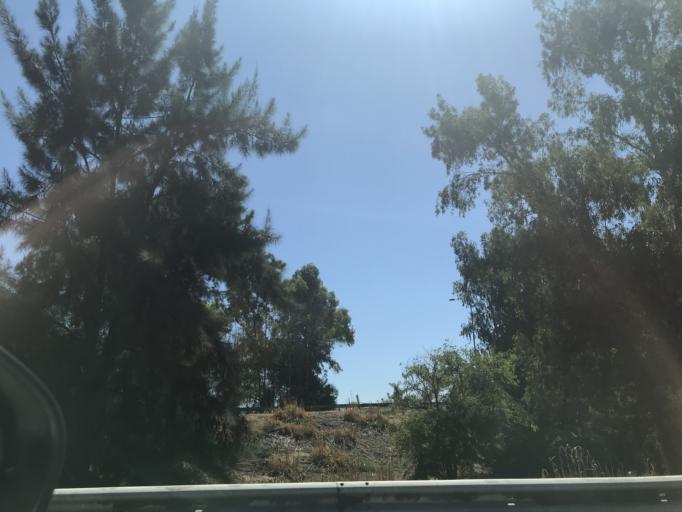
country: TR
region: Aydin
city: Aydin
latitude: 37.8197
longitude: 27.8474
